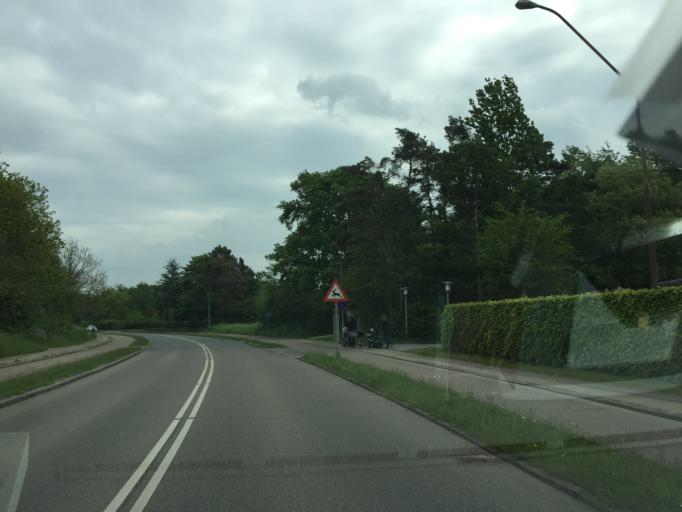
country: DK
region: South Denmark
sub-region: Sonderborg Kommune
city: Sonderborg
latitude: 54.8971
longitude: 9.8148
